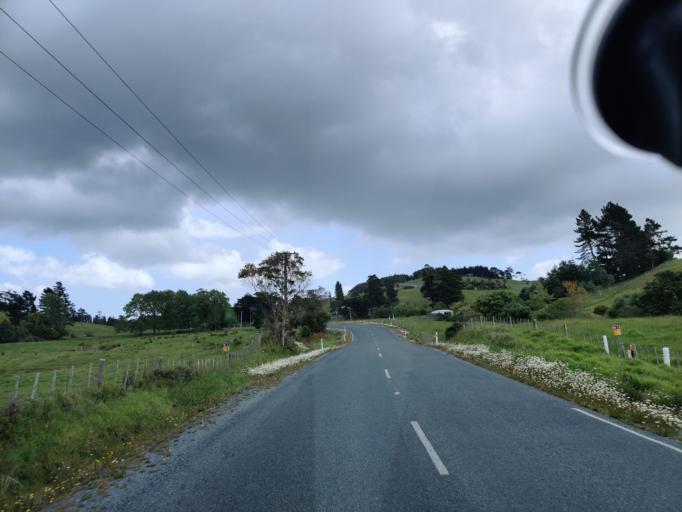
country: NZ
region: Auckland
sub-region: Auckland
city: Wellsford
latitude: -36.2846
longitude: 174.5515
